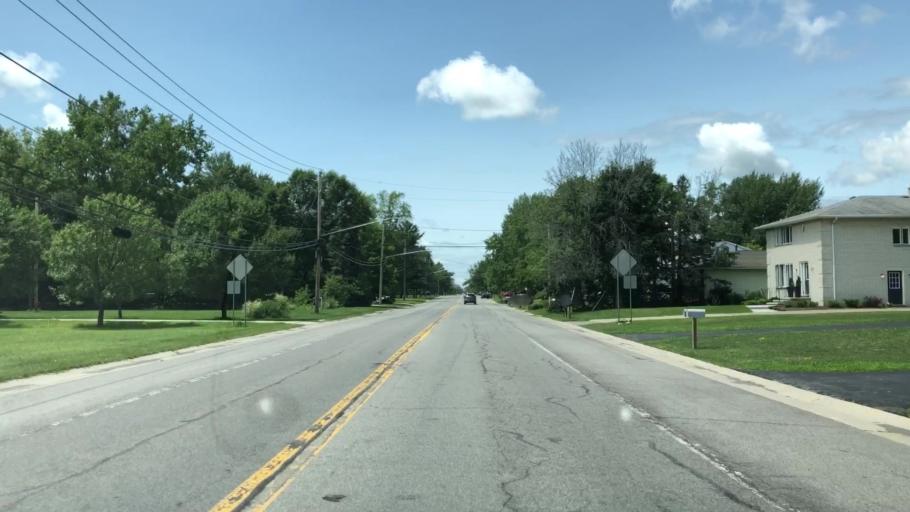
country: US
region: New York
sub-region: Erie County
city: Orchard Park
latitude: 42.8113
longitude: -78.7274
